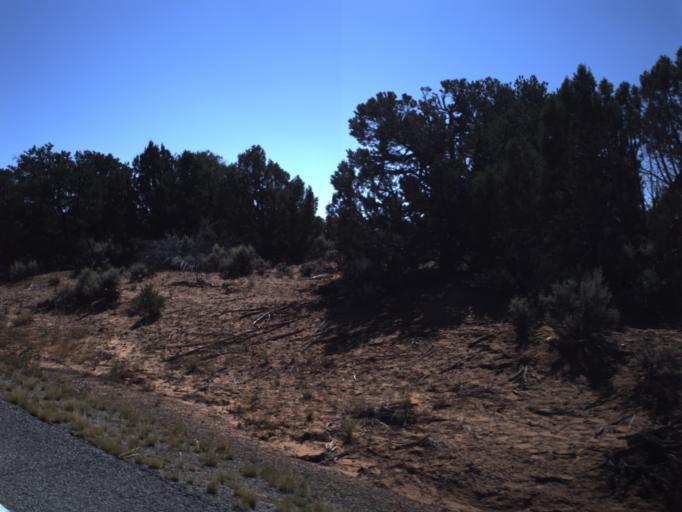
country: US
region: Utah
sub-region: San Juan County
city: Blanding
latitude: 37.5584
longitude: -110.0038
